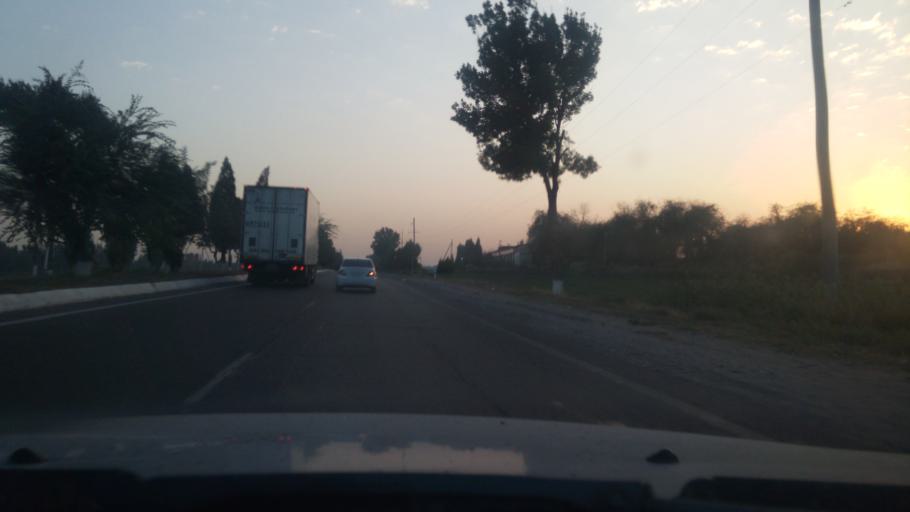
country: UZ
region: Toshkent
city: Zafar
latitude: 41.0315
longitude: 68.8684
